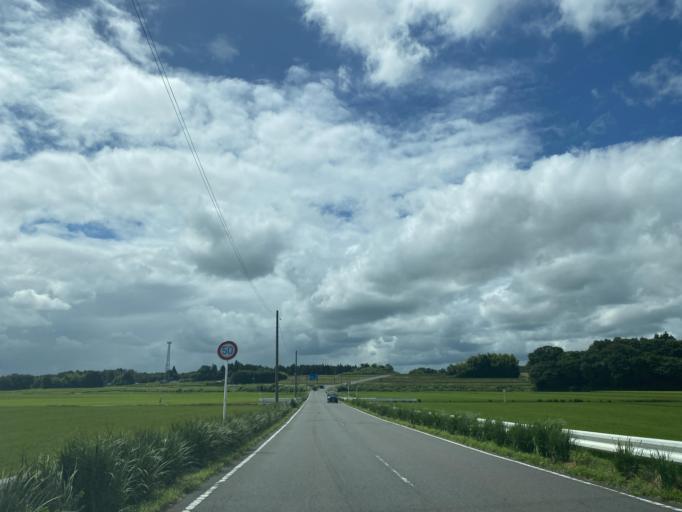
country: JP
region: Fukushima
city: Koriyama
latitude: 37.3711
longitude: 140.2940
